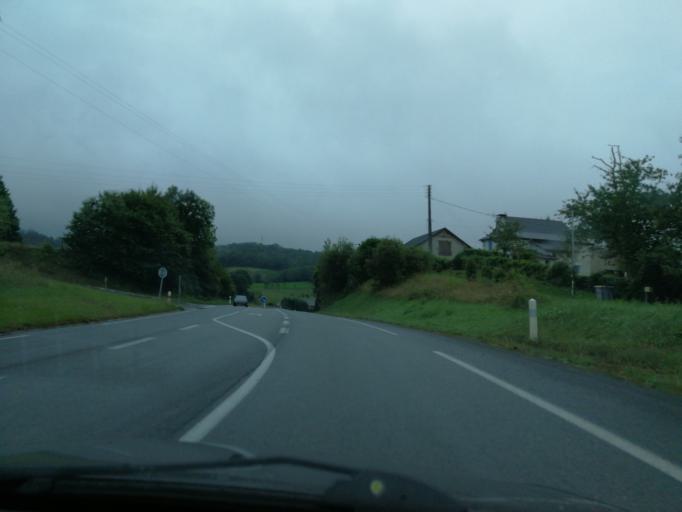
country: FR
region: Aquitaine
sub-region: Departement des Pyrenees-Atlantiques
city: Arudy
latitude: 43.1712
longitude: -0.4416
